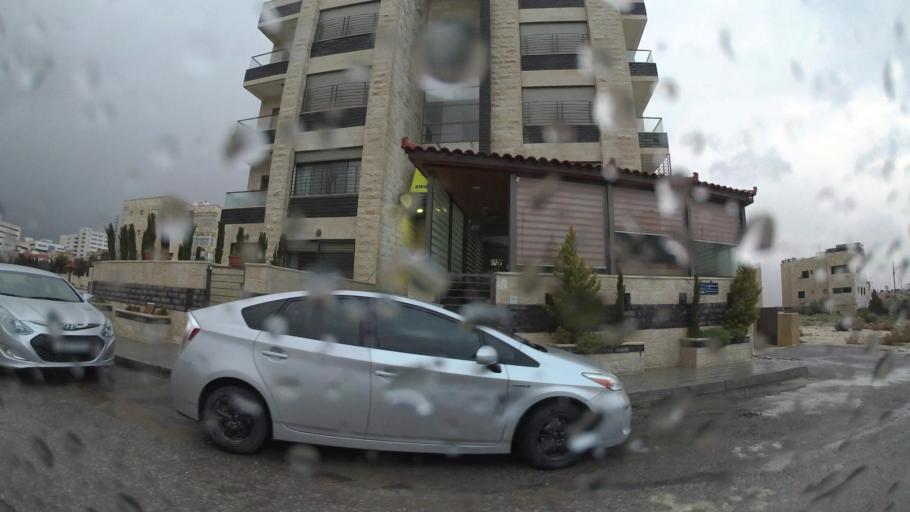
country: JO
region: Amman
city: Amman
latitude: 31.9971
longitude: 35.9209
